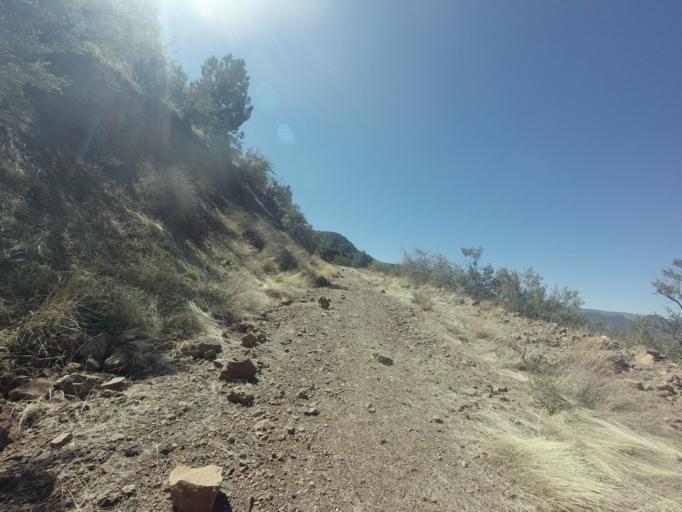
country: US
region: Arizona
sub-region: Gila County
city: Pine
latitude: 34.4033
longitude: -111.6086
